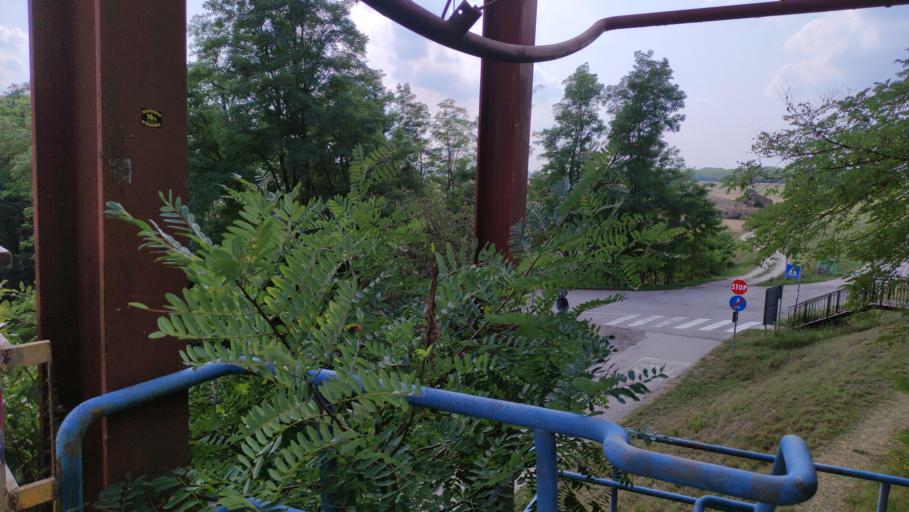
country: IT
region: Emilia-Romagna
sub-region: Provincia di Ferrara
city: Ro
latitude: 44.9569
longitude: 11.7563
